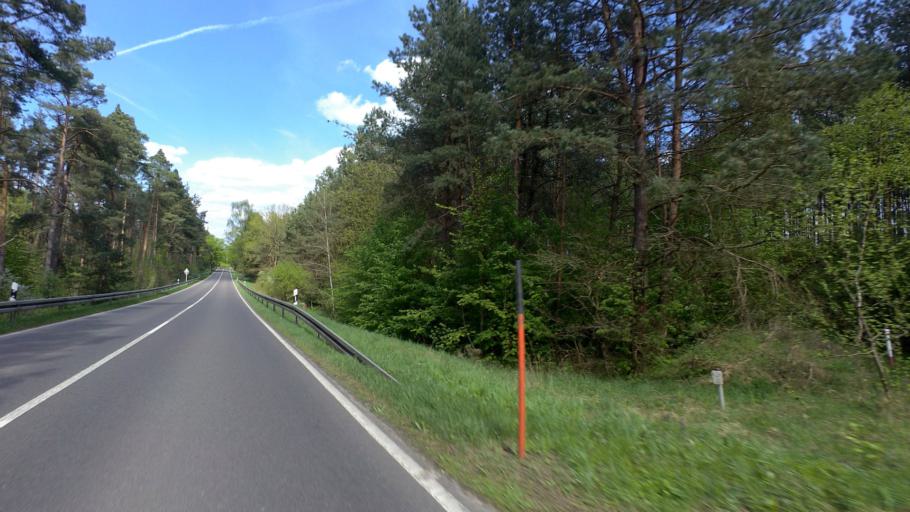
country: DE
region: Brandenburg
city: Milmersdorf
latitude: 53.0852
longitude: 13.6248
